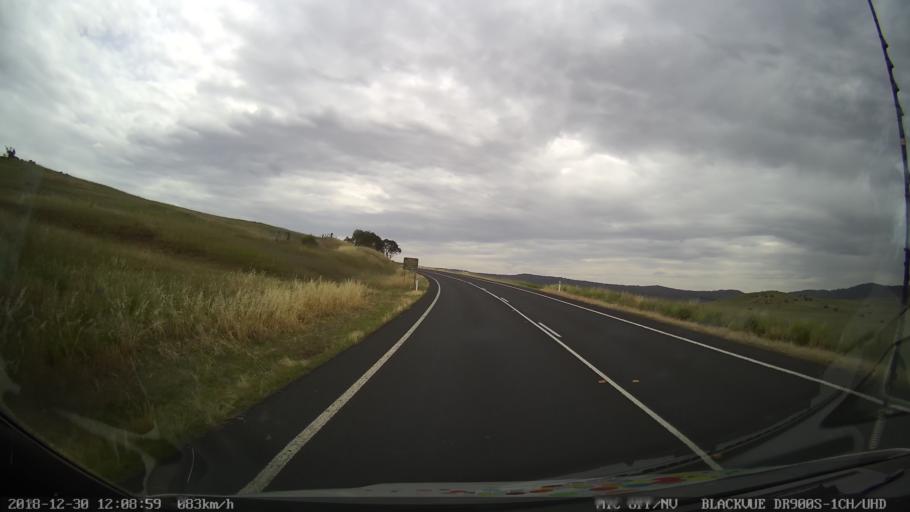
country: AU
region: New South Wales
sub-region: Snowy River
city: Jindabyne
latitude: -36.3898
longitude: 148.5974
